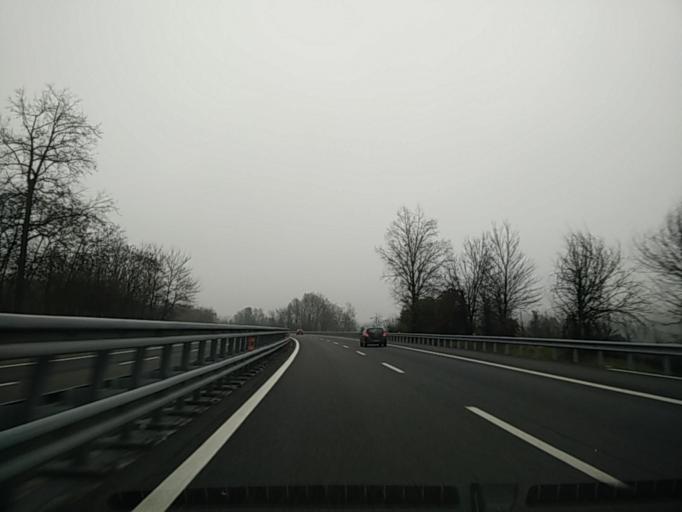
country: IT
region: Piedmont
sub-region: Provincia di Asti
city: Tigliole
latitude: 44.9019
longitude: 8.0645
